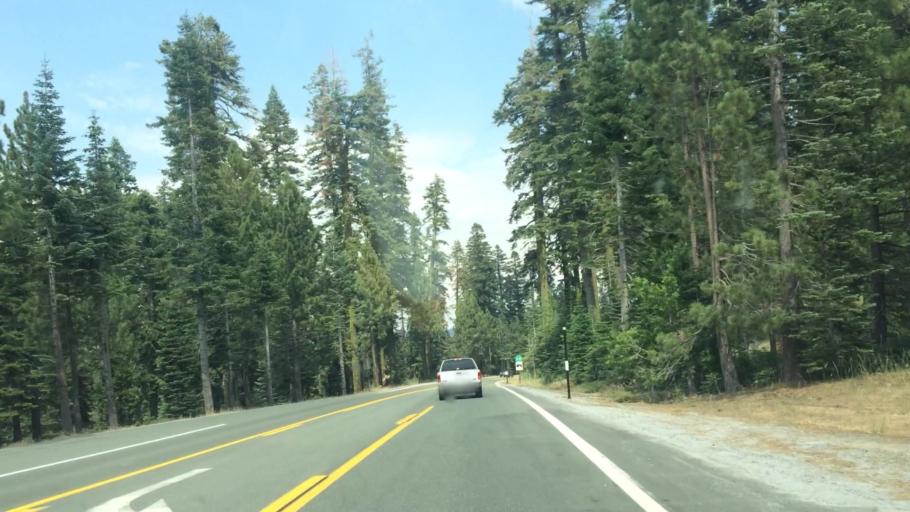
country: US
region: California
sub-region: Amador County
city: Pioneer
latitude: 38.5480
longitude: -120.3064
